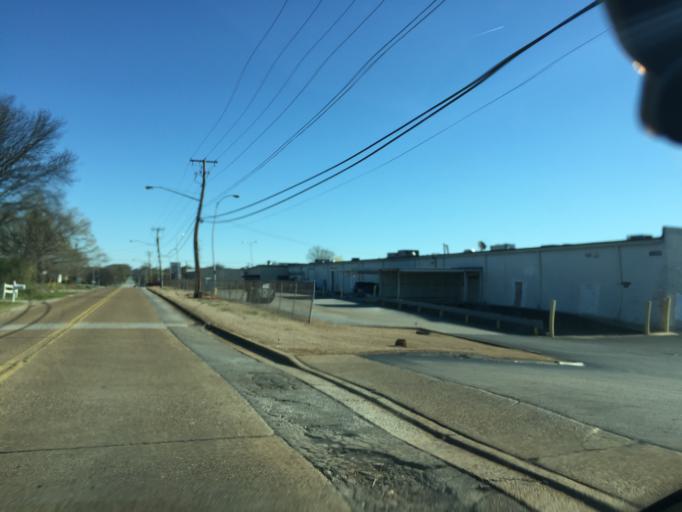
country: US
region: Tennessee
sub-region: Hamilton County
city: East Brainerd
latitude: 35.0437
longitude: -85.1677
